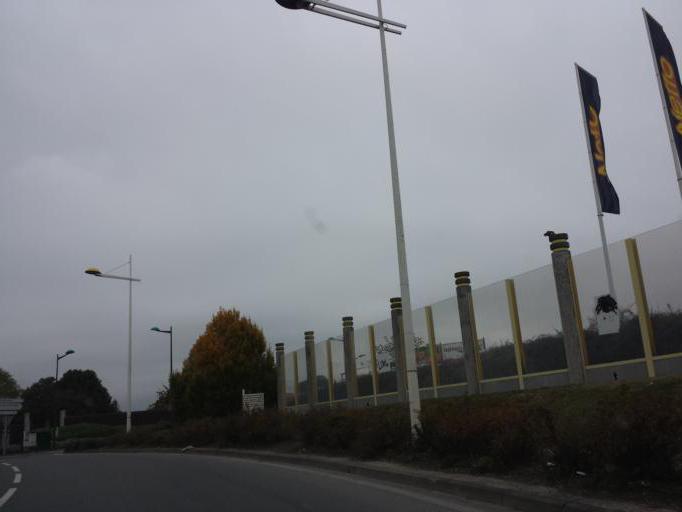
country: FR
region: Poitou-Charentes
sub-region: Departement de la Charente
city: Angouleme
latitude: 45.6269
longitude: 0.1542
